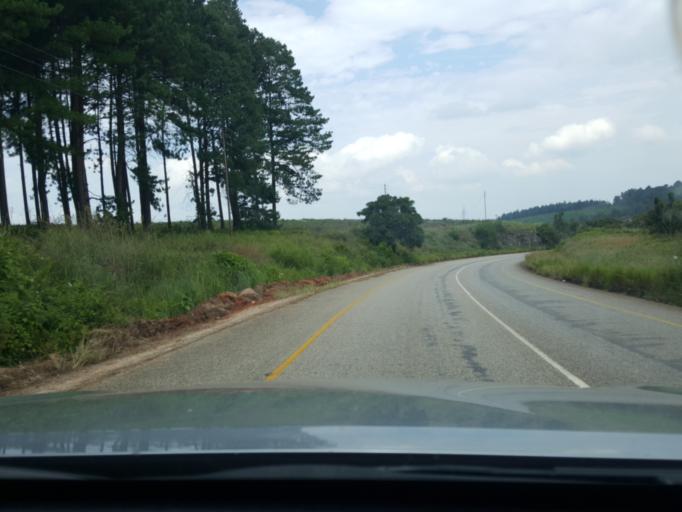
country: ZA
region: Mpumalanga
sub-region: Ehlanzeni District
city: White River
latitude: -25.1986
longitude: 30.9369
